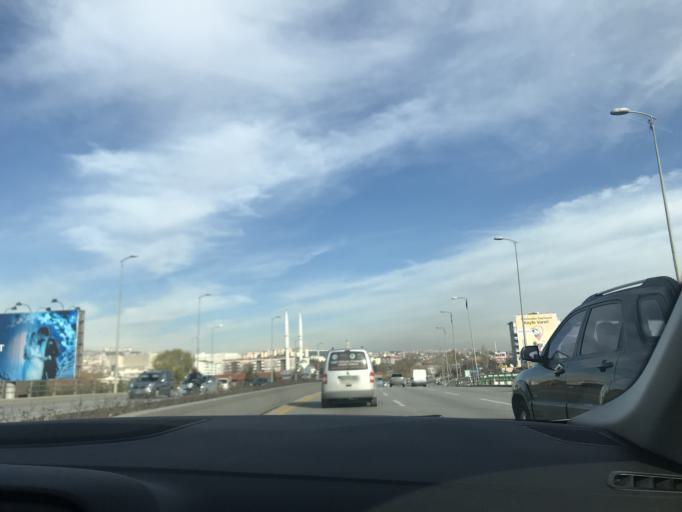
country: TR
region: Ankara
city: Ankara
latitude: 39.9513
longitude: 32.8355
